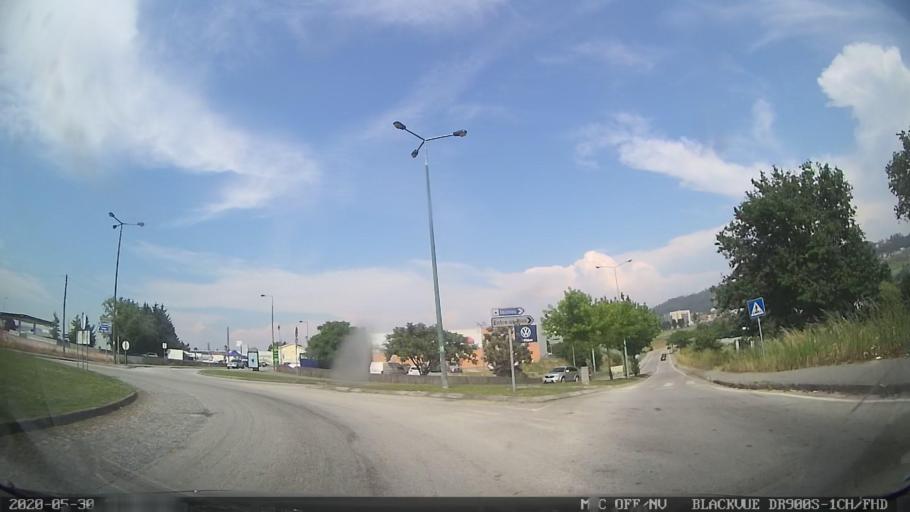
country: PT
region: Porto
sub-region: Paredes
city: Paredes
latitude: 41.1912
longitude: -8.3073
